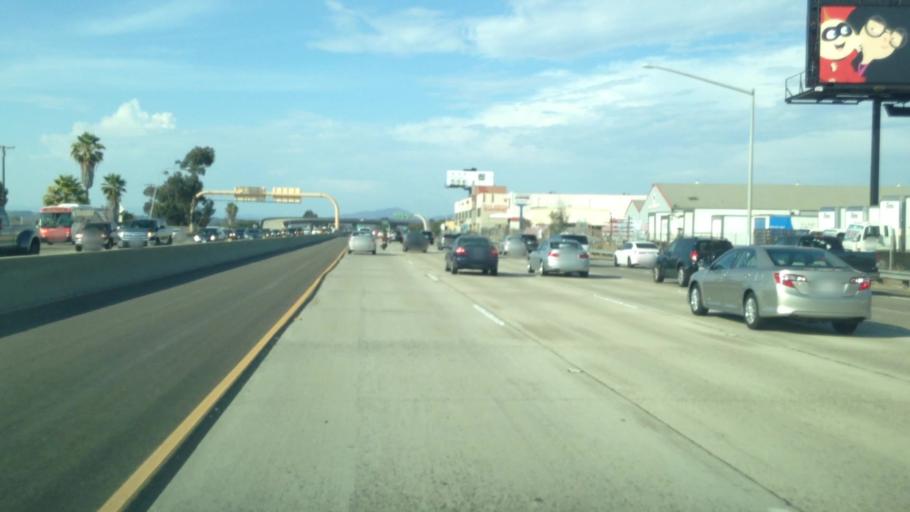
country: US
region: California
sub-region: San Diego County
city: San Diego
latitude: 32.8370
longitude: -117.1372
